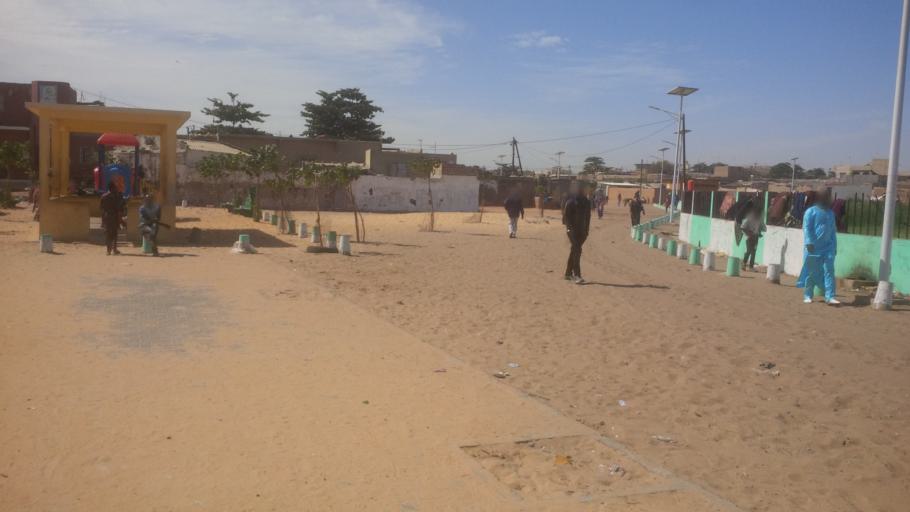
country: SN
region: Dakar
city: Pikine
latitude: 14.7734
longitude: -17.3735
